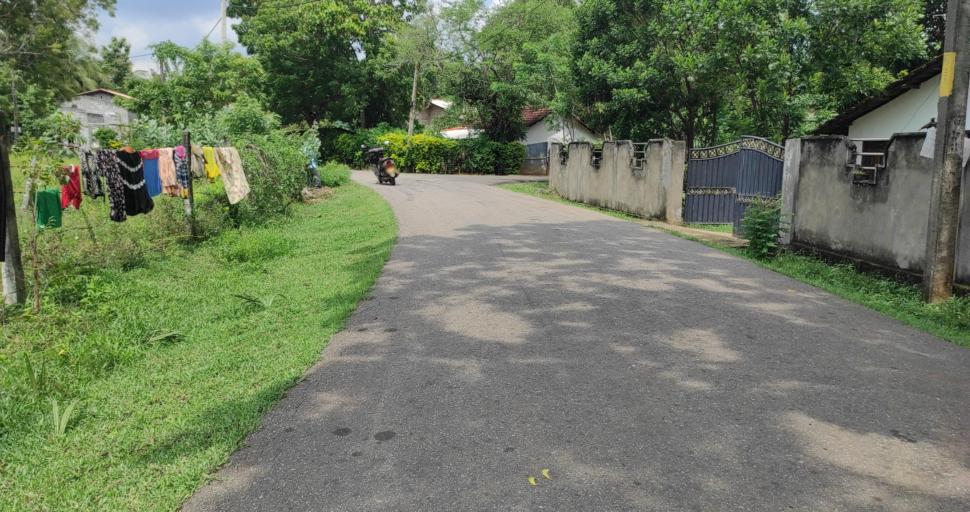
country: LK
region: Eastern Province
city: Trincomalee
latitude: 8.3802
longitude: 81.0144
